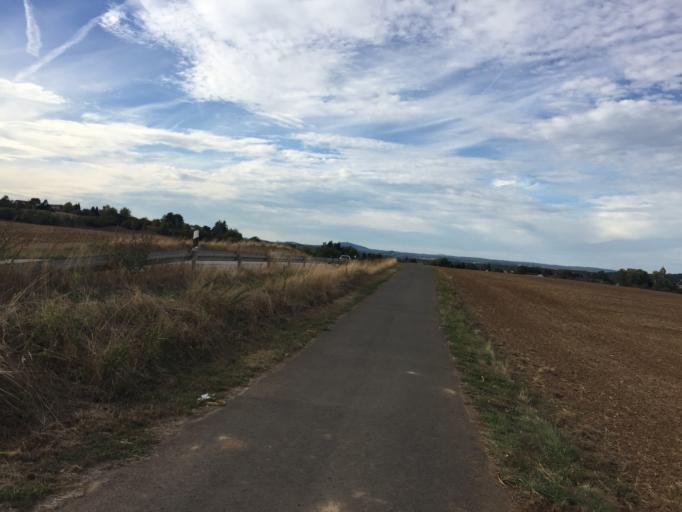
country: DE
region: Hesse
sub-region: Regierungsbezirk Giessen
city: Langgons
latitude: 50.5258
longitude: 8.7169
